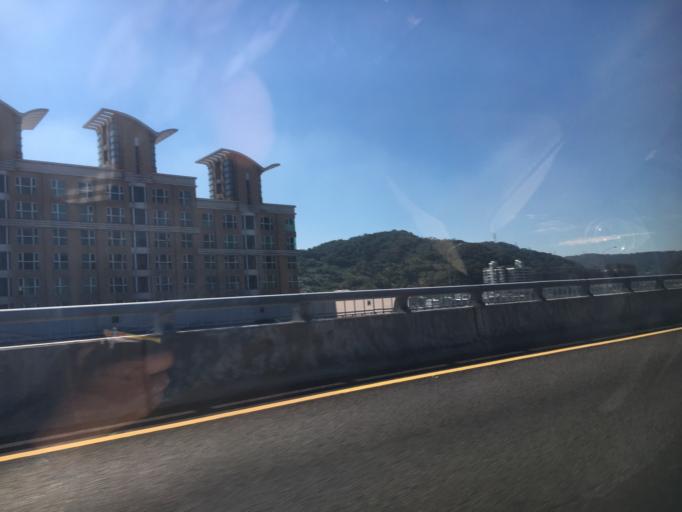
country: TW
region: Taipei
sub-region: Taipei
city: Banqiao
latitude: 25.0687
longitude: 121.4325
